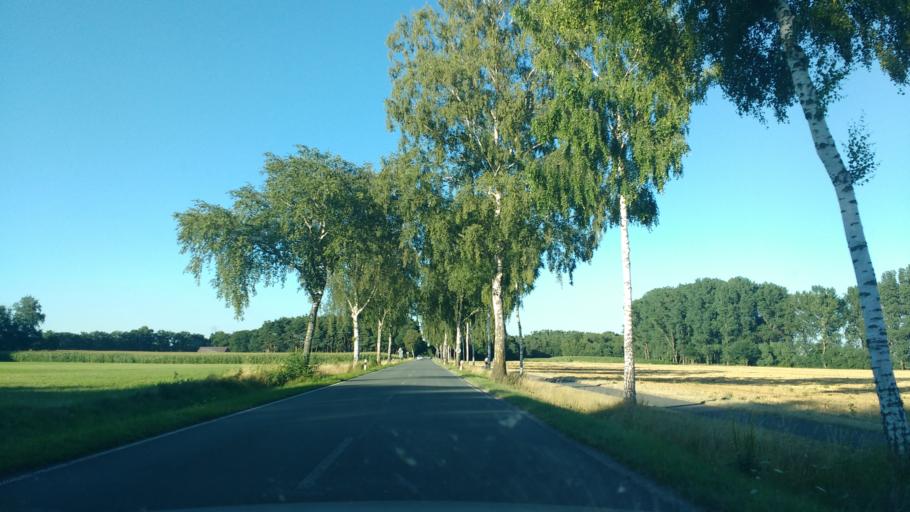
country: DE
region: North Rhine-Westphalia
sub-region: Regierungsbezirk Arnsberg
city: Lippstadt
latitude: 51.6979
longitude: 8.4084
